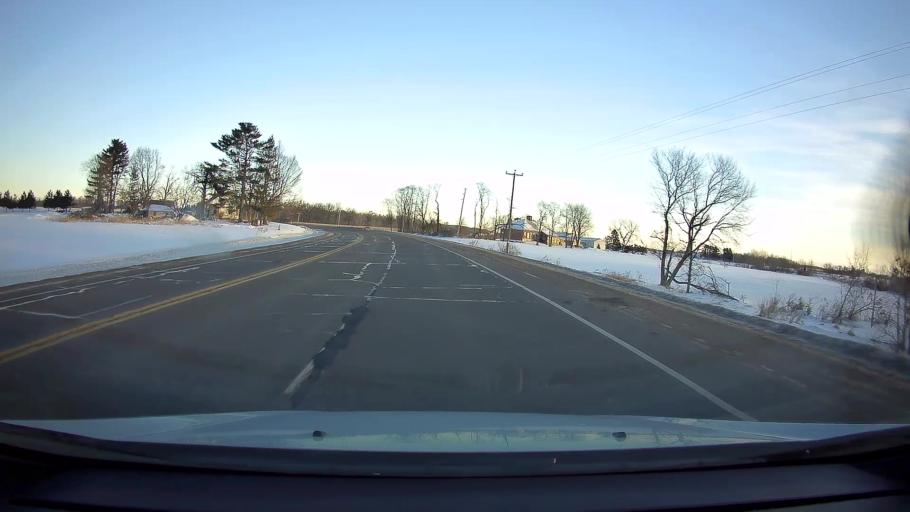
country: US
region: Wisconsin
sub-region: Barron County
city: Cumberland
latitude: 45.4939
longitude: -92.0537
